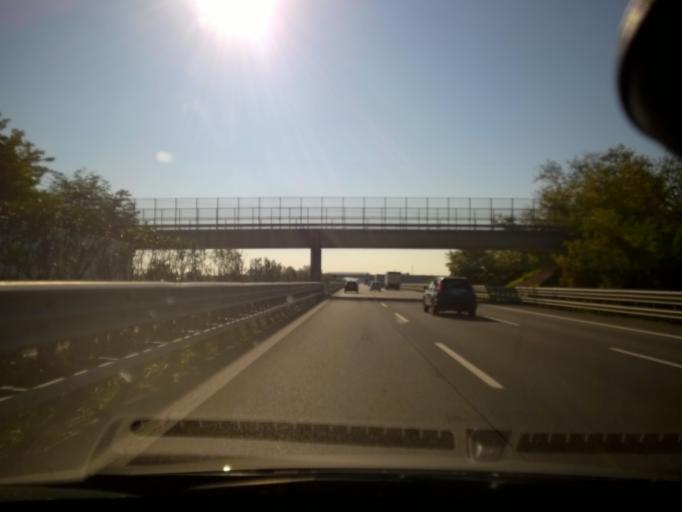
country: IT
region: Lombardy
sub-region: Provincia di Brescia
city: San Zeno Naviglio
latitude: 45.4849
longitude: 10.2254
